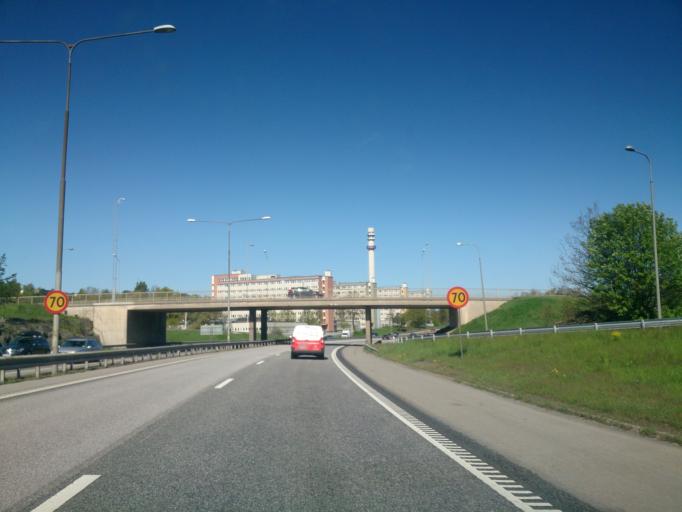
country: SE
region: Stockholm
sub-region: Stockholms Kommun
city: Arsta
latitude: 59.2439
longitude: 18.1081
